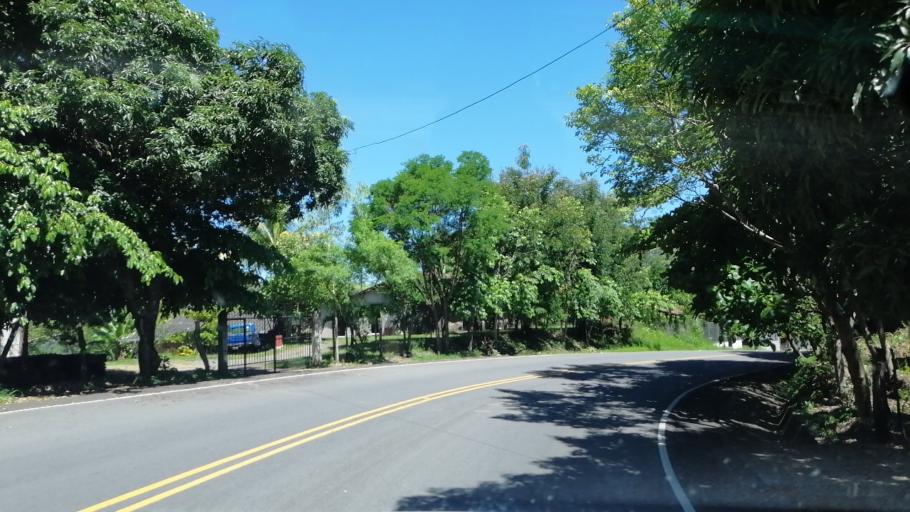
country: SV
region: Morazan
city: Cacaopera
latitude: 13.8133
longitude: -88.1701
